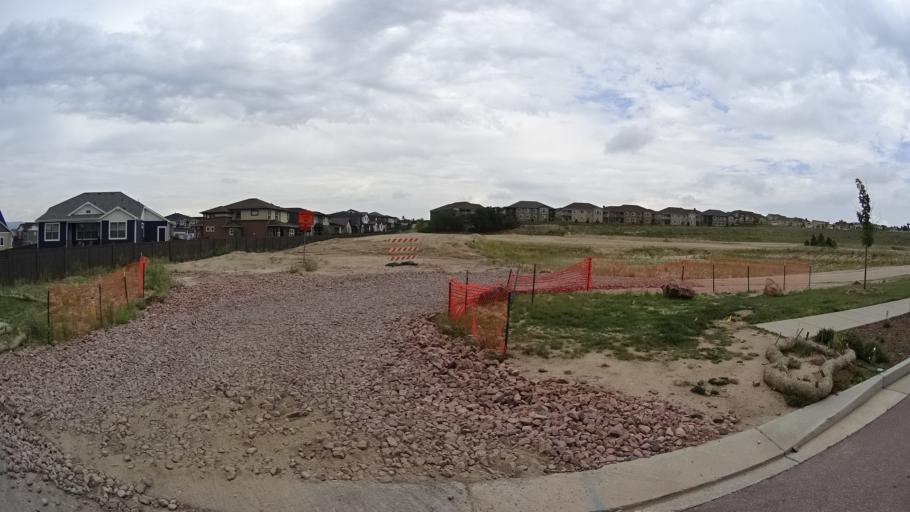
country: US
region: Colorado
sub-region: El Paso County
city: Gleneagle
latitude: 39.0000
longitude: -104.8026
